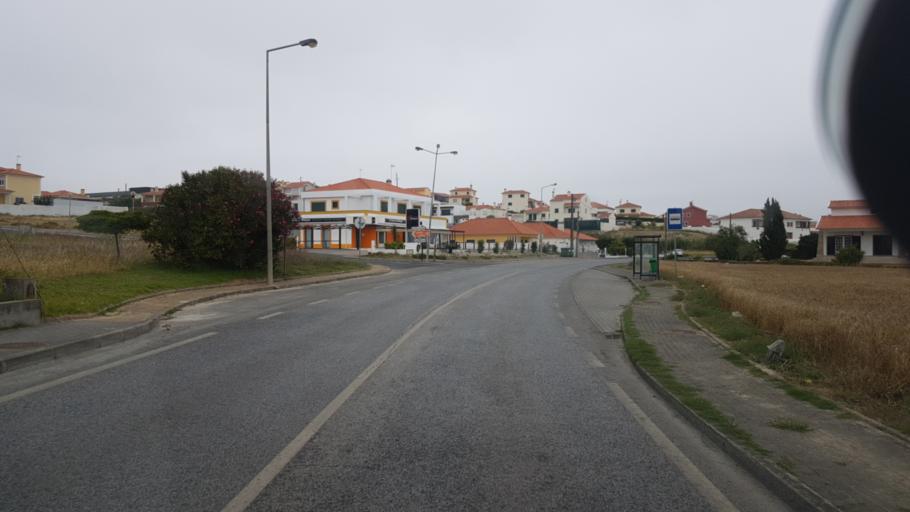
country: PT
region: Lisbon
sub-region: Torres Vedras
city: Silveira
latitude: 39.0924
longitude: -9.3271
